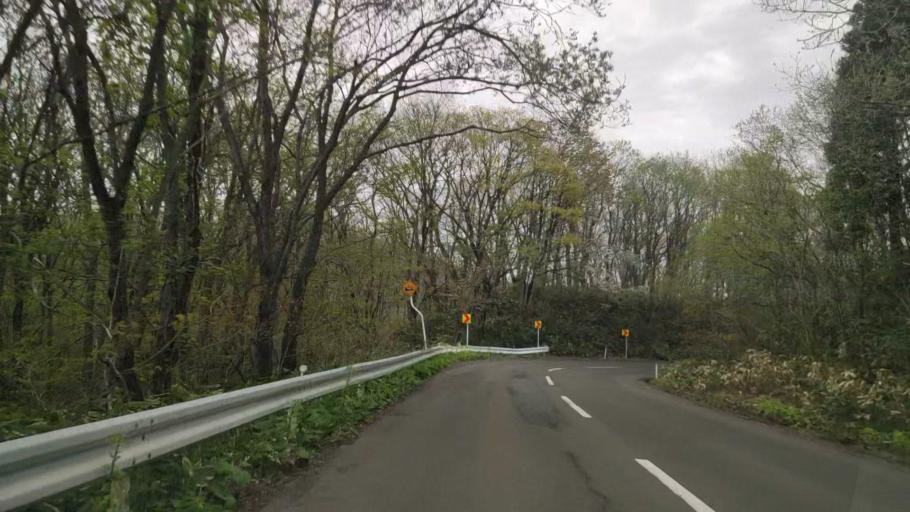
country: JP
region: Akita
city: Hanawa
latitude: 40.3754
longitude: 140.7899
